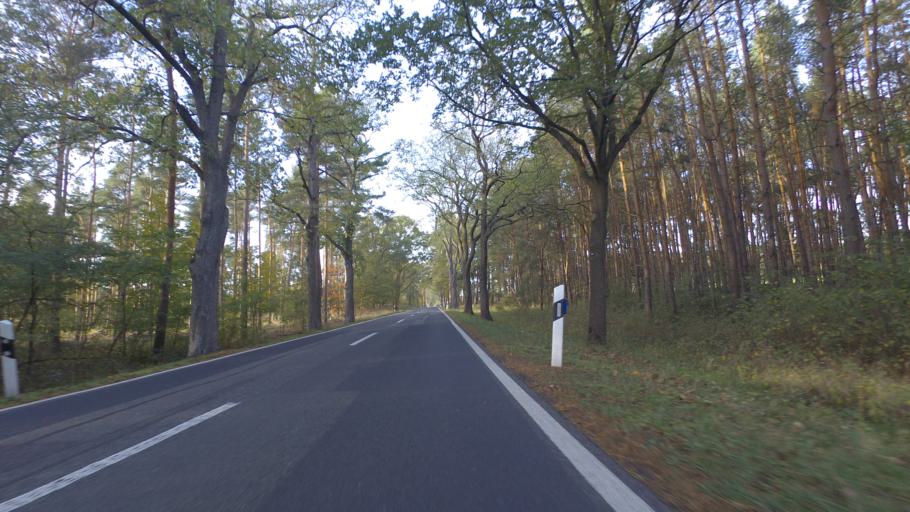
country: DE
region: Brandenburg
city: Sperenberg
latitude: 52.1997
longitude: 13.3114
